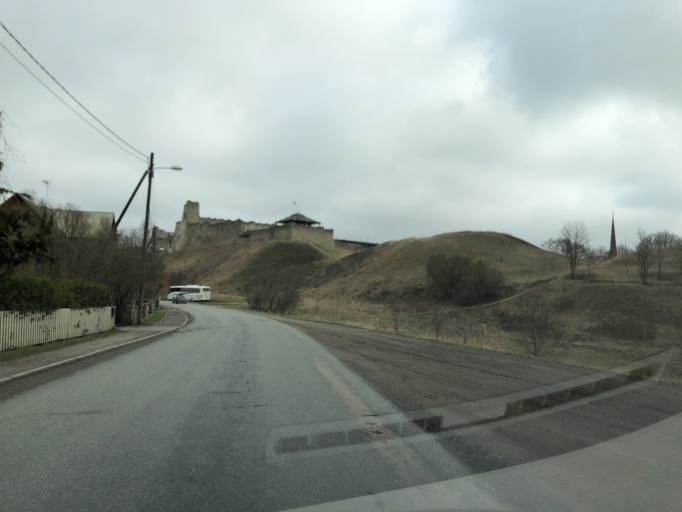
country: EE
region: Laeaene-Virumaa
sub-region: Rakvere linn
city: Rakvere
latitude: 59.3458
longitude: 26.3496
